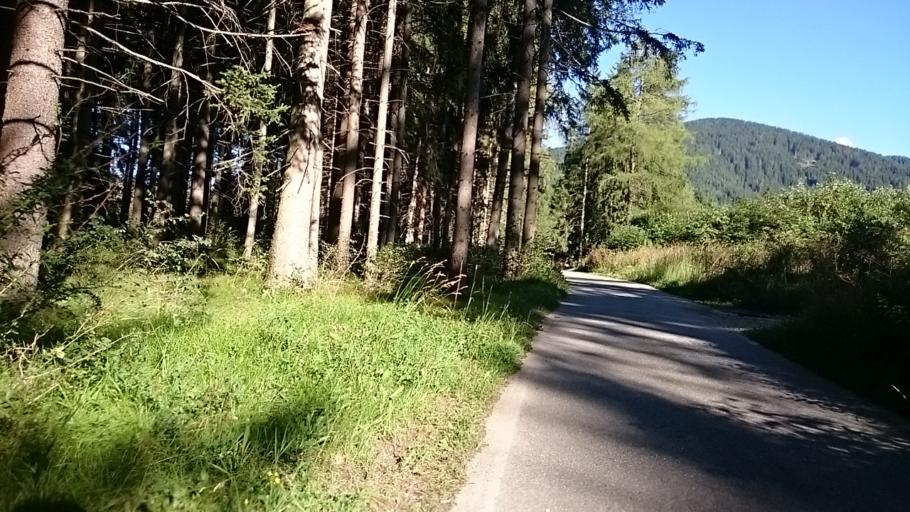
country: IT
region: Trentino-Alto Adige
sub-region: Bolzano
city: Braies
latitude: 46.7387
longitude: 12.1322
